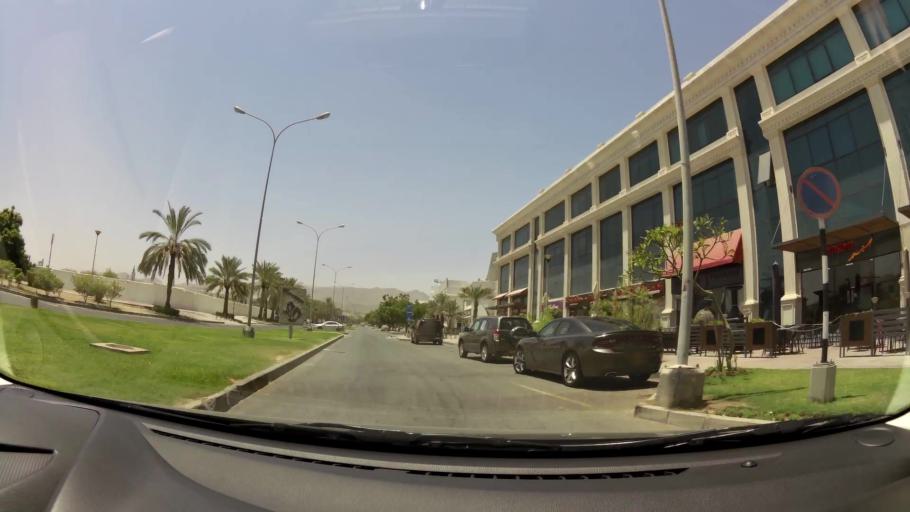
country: OM
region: Muhafazat Masqat
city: Bawshar
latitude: 23.6125
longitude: 58.4540
